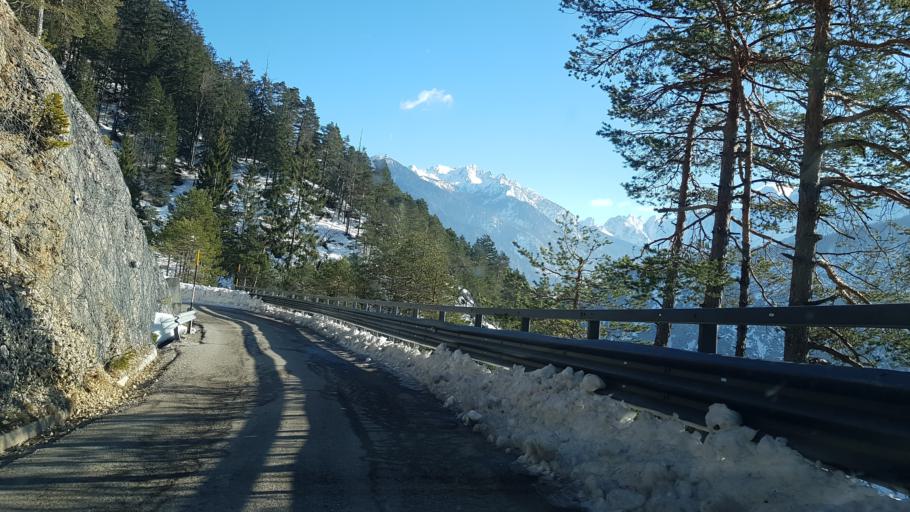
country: IT
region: Friuli Venezia Giulia
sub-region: Provincia di Udine
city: Malborghetto
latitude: 46.5166
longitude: 13.4727
